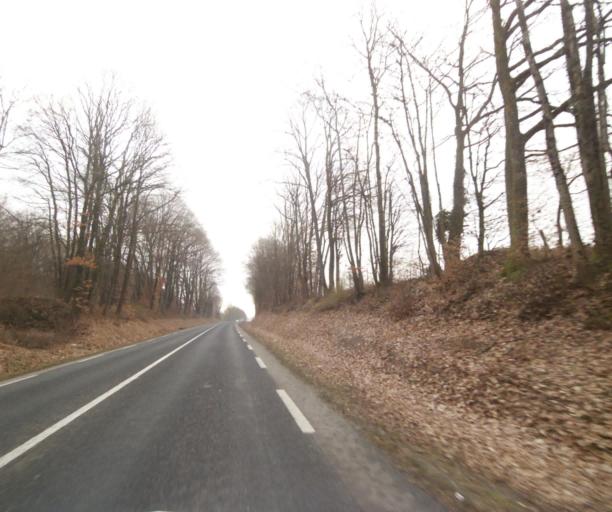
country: FR
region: Champagne-Ardenne
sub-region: Departement de la Haute-Marne
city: Bettancourt-la-Ferree
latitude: 48.6372
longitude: 4.9918
